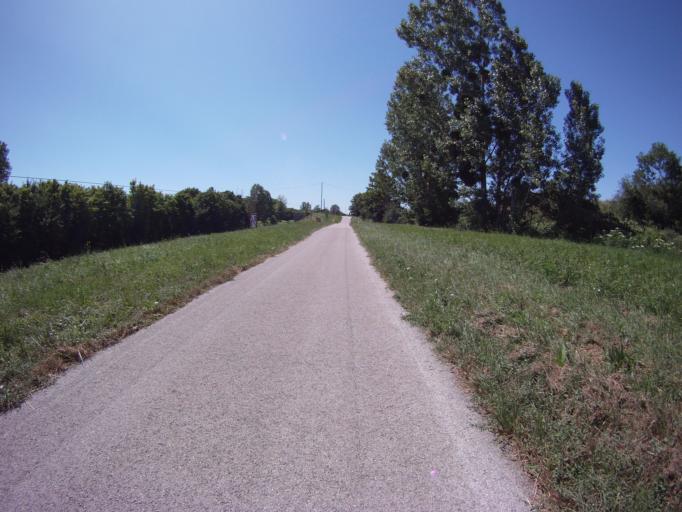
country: FR
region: Champagne-Ardenne
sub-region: Departement de la Marne
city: Damery
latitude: 49.0746
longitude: 3.8488
